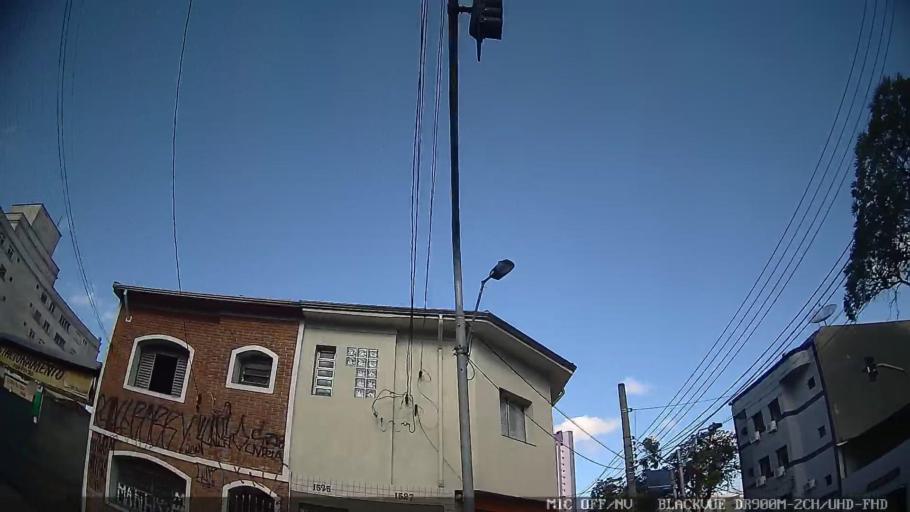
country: BR
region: Sao Paulo
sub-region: Sao Caetano Do Sul
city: Sao Caetano do Sul
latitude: -23.5970
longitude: -46.6021
